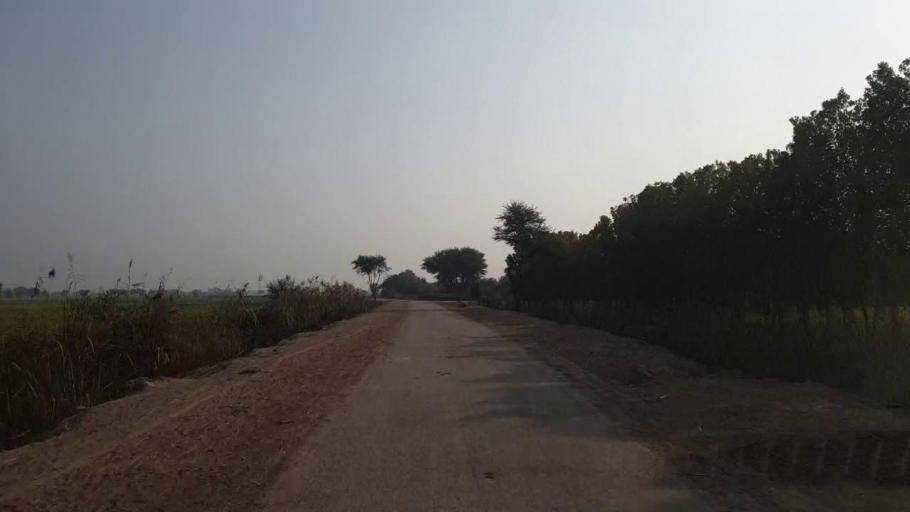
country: PK
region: Sindh
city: Shahdadpur
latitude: 25.9641
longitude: 68.5235
